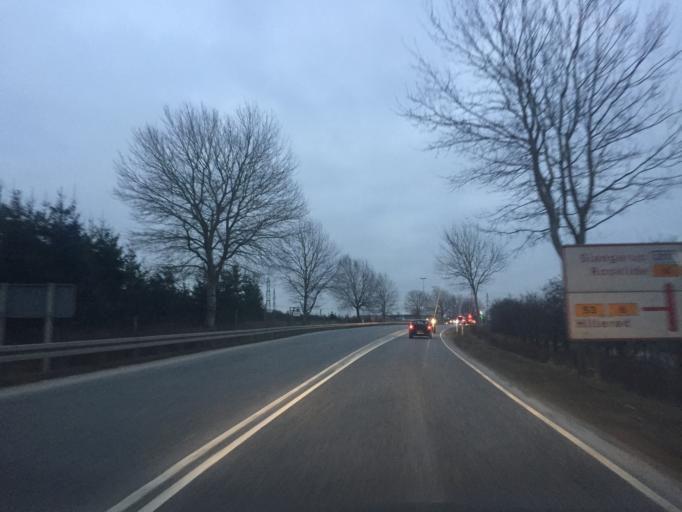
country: DK
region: Capital Region
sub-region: Frederikssund Kommune
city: Slangerup
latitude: 55.8486
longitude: 12.1460
